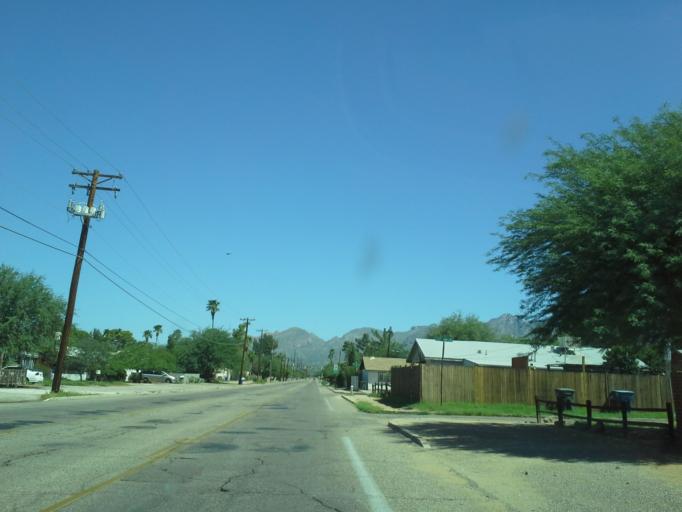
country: US
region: Arizona
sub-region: Pima County
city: Tucson
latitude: 32.2544
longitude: -110.9353
